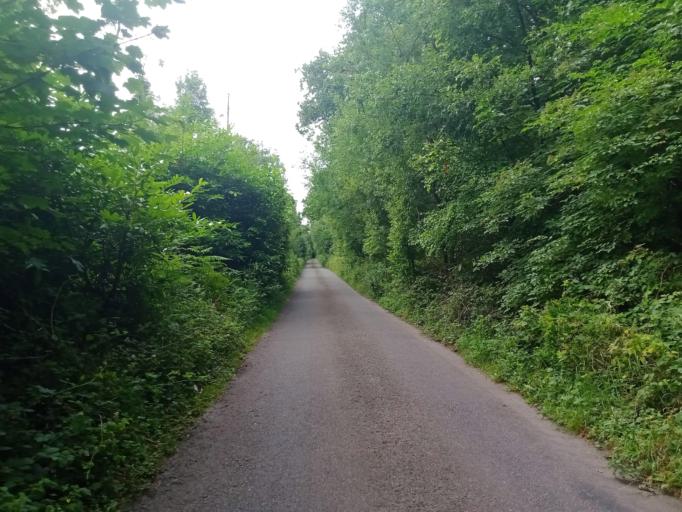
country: IE
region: Leinster
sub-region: Laois
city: Abbeyleix
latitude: 52.9031
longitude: -7.3614
